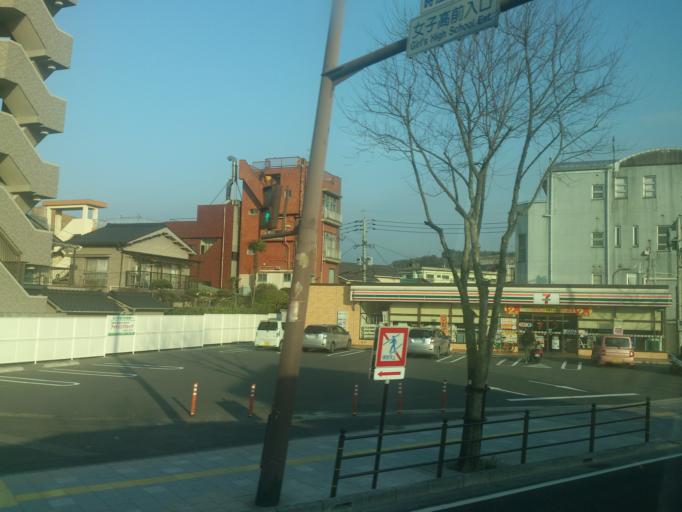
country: JP
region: Kagoshima
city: Kagoshima-shi
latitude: 31.6060
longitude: 130.5370
